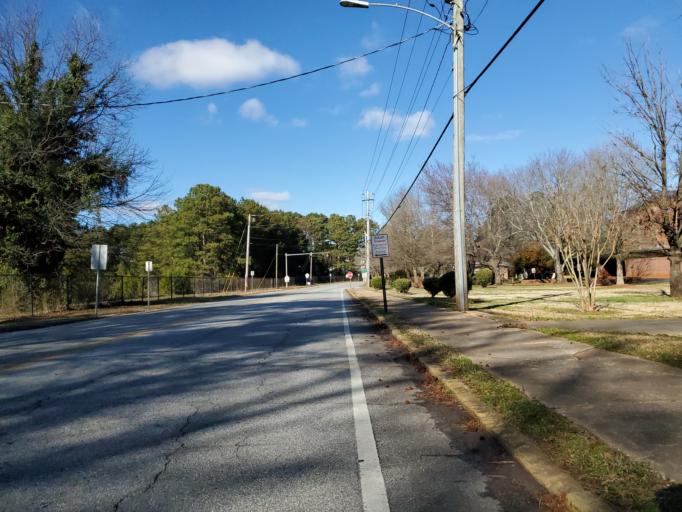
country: US
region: Georgia
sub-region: DeKalb County
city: Belvedere Park
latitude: 33.7600
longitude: -84.2684
